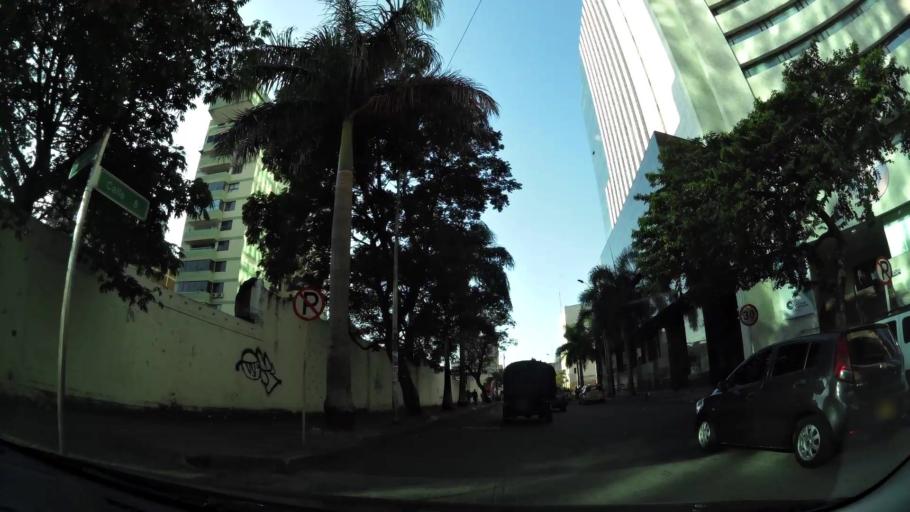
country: CO
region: Valle del Cauca
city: Cali
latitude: 3.4517
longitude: -76.5355
